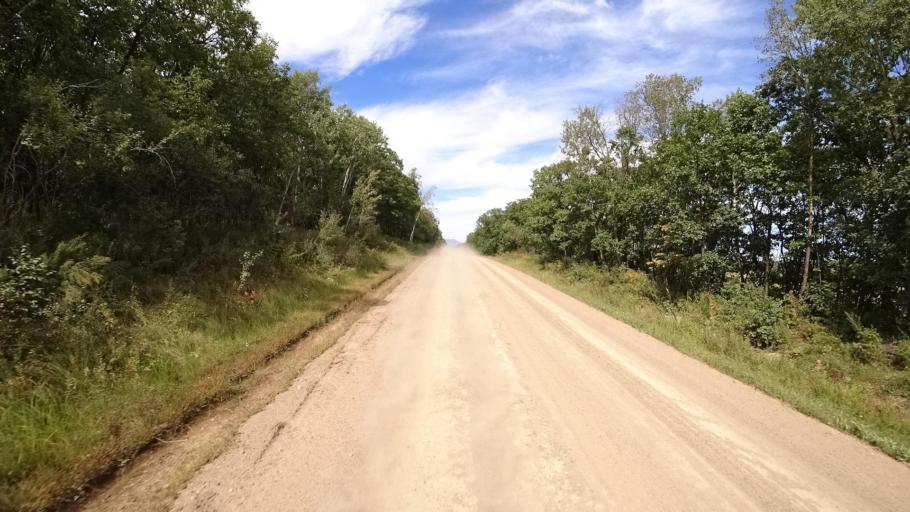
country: RU
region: Primorskiy
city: Yakovlevka
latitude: 44.6041
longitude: 133.6031
